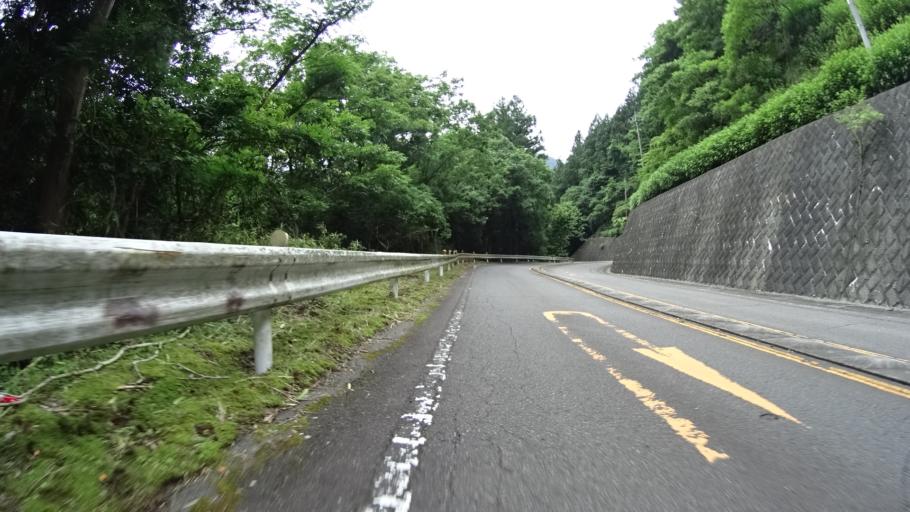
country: JP
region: Kanagawa
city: Hadano
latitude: 35.4989
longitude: 139.2308
